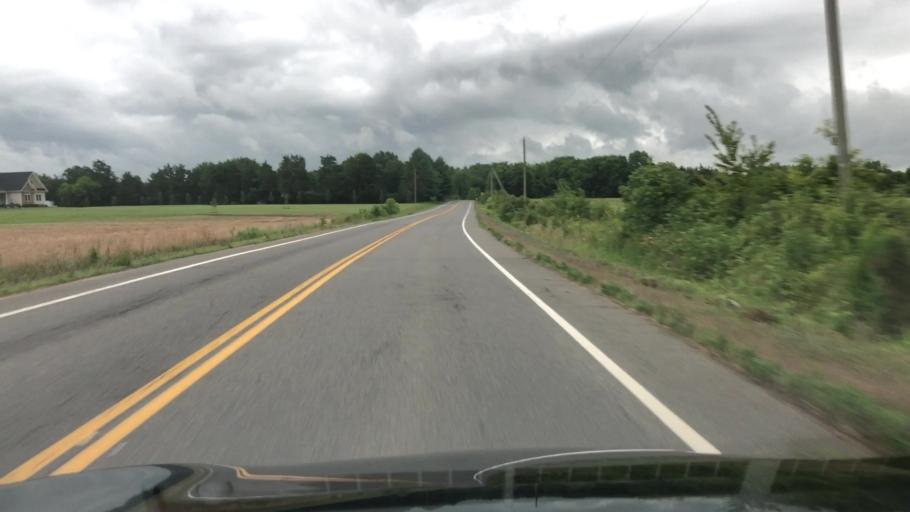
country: US
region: Virginia
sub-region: Prince William County
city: Nokesville
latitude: 38.6168
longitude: -77.6047
